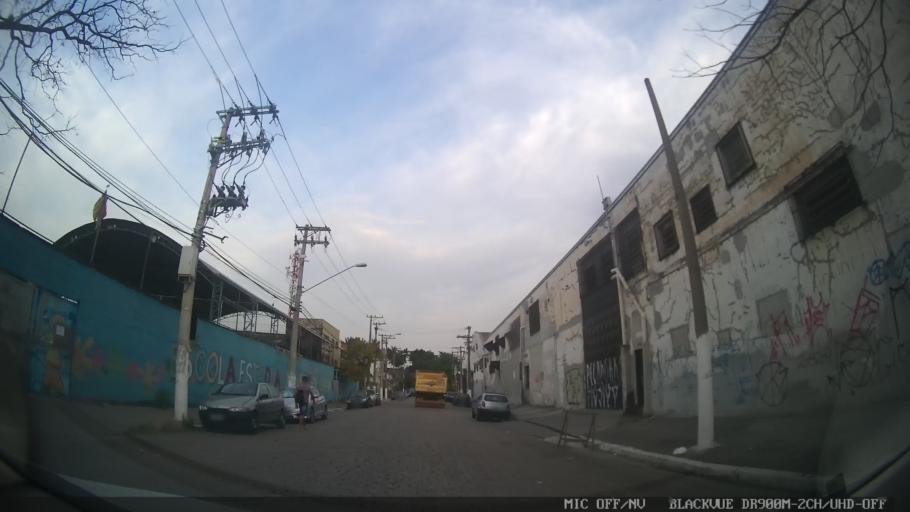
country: BR
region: Sao Paulo
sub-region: Sao Caetano Do Sul
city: Sao Caetano do Sul
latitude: -23.5989
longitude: -46.5917
